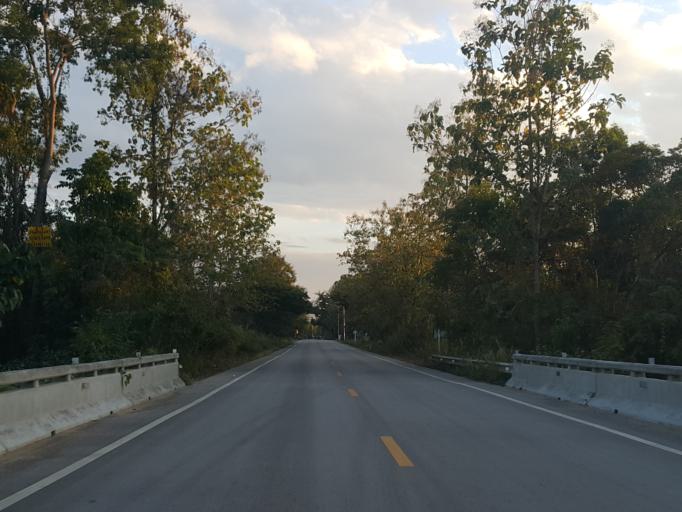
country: TH
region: Lampang
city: Mae Mo
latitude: 18.4549
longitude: 99.6344
